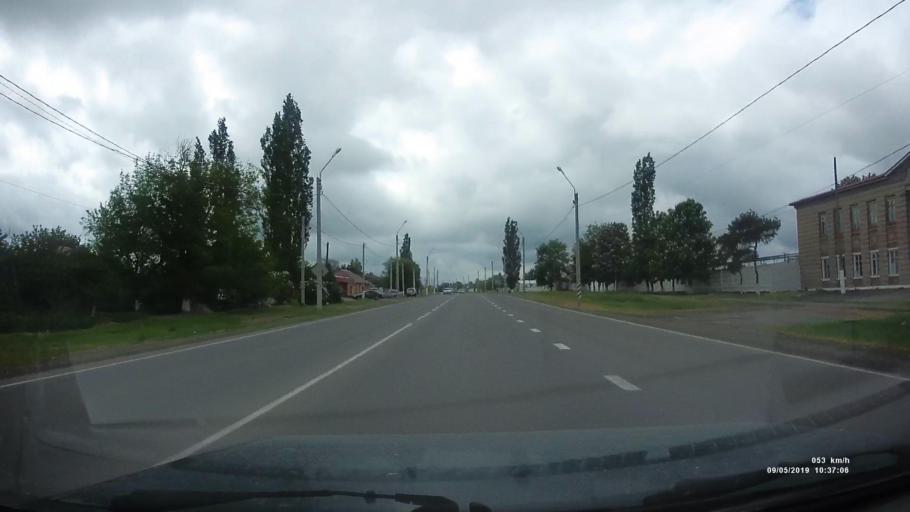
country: RU
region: Rostov
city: Peshkovo
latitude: 47.0231
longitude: 39.4045
